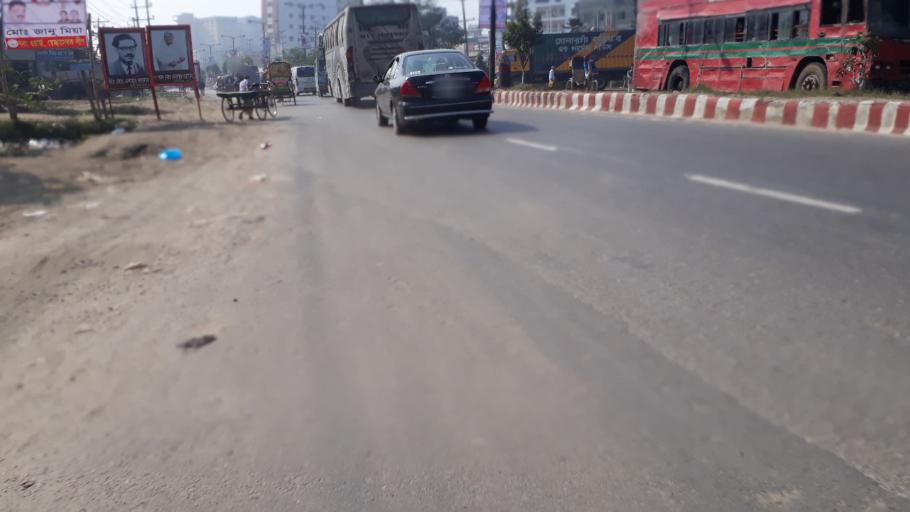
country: BD
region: Dhaka
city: Tungi
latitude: 23.8542
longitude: 90.2601
